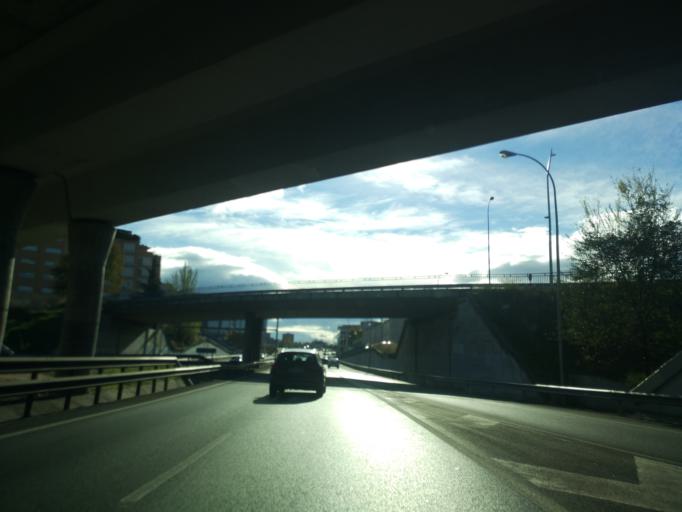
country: ES
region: Madrid
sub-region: Provincia de Madrid
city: Usera
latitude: 40.3809
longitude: -3.6915
